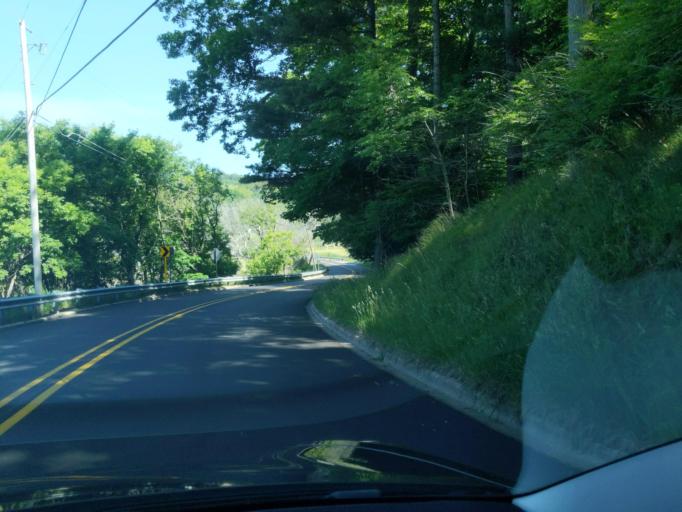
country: US
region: Michigan
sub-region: Muskegon County
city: Montague
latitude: 43.3833
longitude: -86.4260
